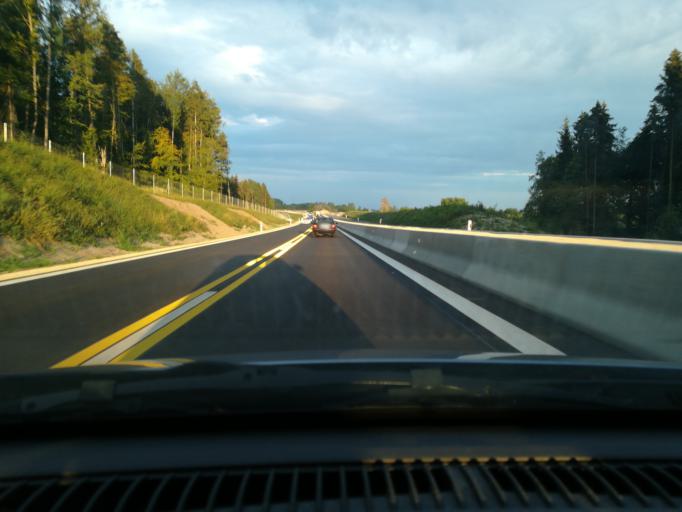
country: DE
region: Baden-Wuerttemberg
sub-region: Freiburg Region
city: Allensbach
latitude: 47.7300
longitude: 9.0340
